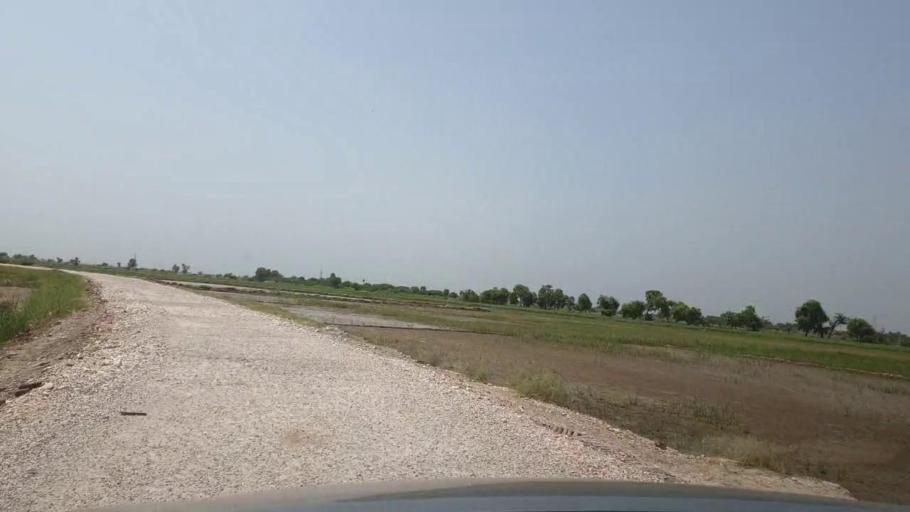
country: PK
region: Sindh
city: Garhi Yasin
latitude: 27.8990
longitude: 68.4987
